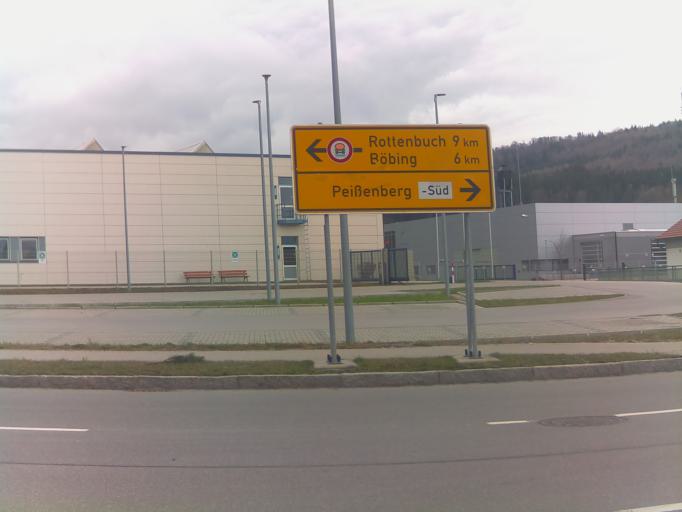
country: DE
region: Bavaria
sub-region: Upper Bavaria
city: Peissenberg
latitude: 47.7815
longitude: 11.0545
